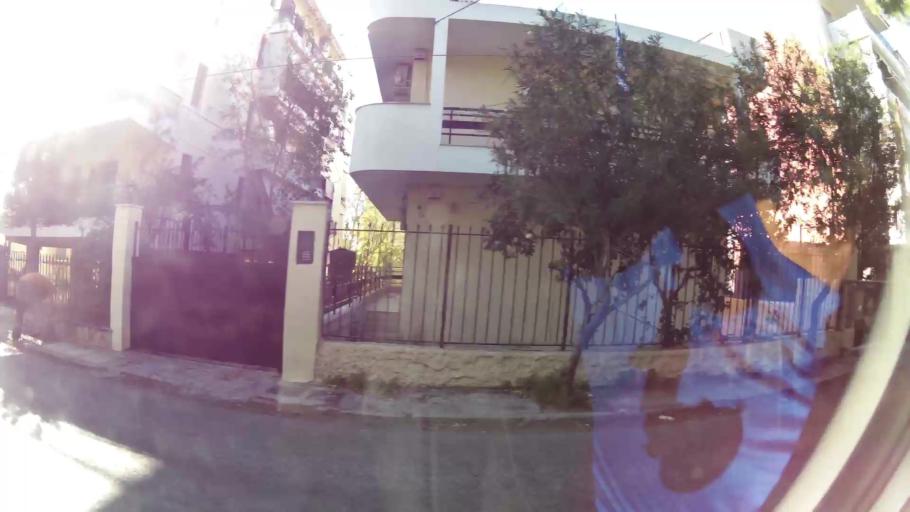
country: GR
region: Attica
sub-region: Nomarchia Athinas
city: Lykovrysi
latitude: 38.0657
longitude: 23.7746
